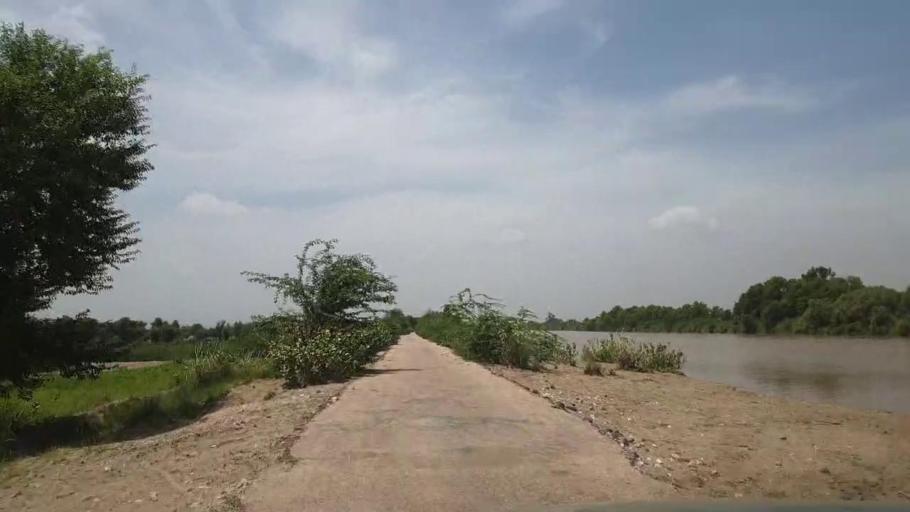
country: PK
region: Sindh
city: Kot Diji
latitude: 27.1323
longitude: 69.0067
